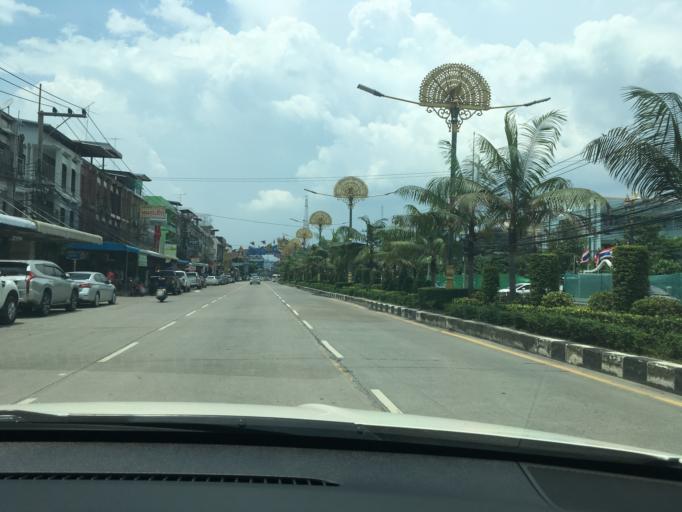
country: TH
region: Chon Buri
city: Chon Buri
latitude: 13.3552
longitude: 100.9774
